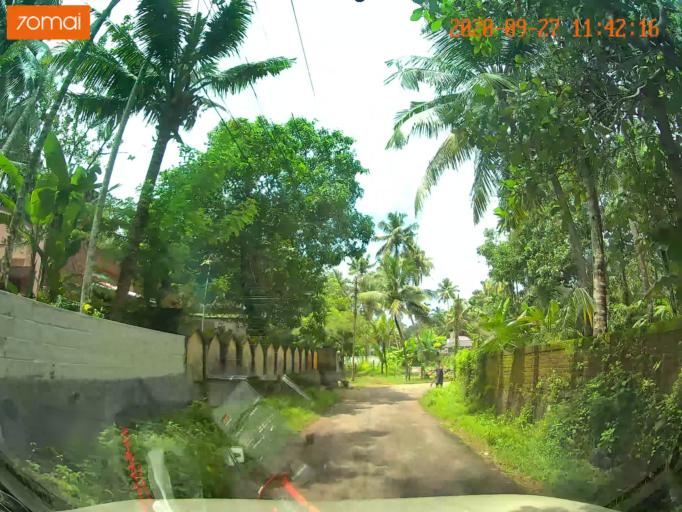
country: IN
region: Kerala
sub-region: Thrissur District
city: Thanniyam
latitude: 10.4715
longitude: 76.1129
